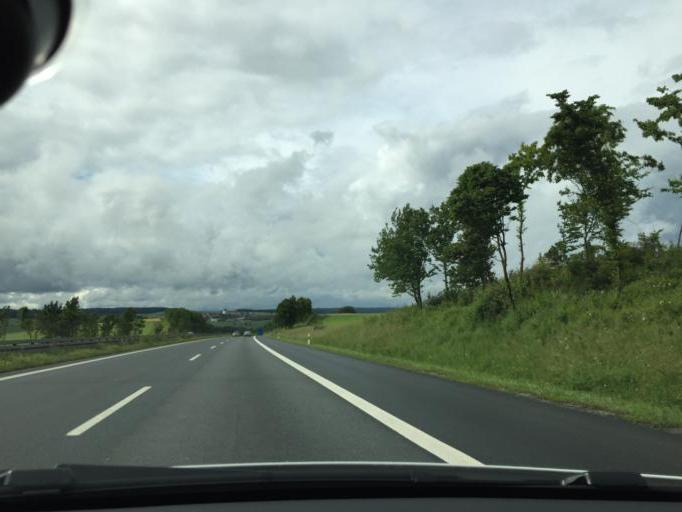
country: DE
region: Bavaria
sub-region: Regierungsbezirk Unterfranken
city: Wasserlosen
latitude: 50.0552
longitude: 10.0531
